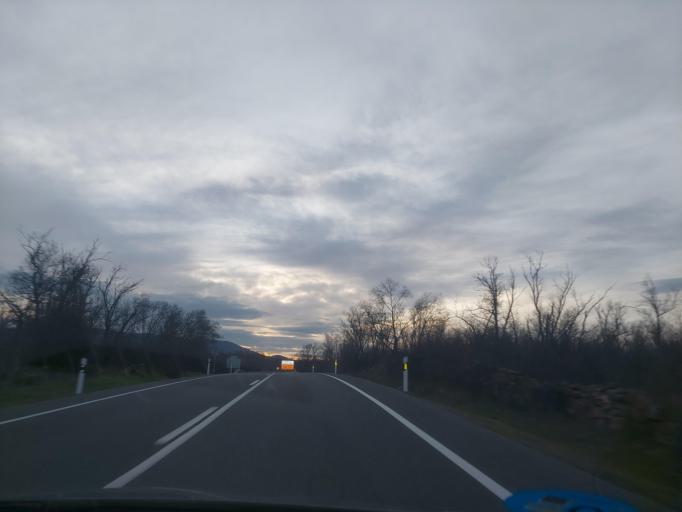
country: ES
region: Castille and Leon
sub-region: Provincia de Segovia
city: Gallegos
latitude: 41.0915
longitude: -3.7816
